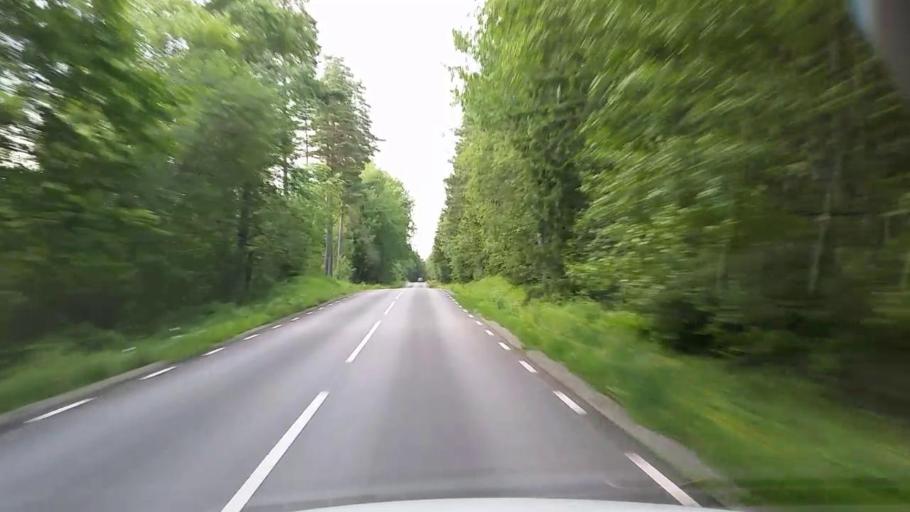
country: SE
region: Vaestmanland
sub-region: Kopings Kommun
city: Kolsva
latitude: 59.7515
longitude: 15.8316
